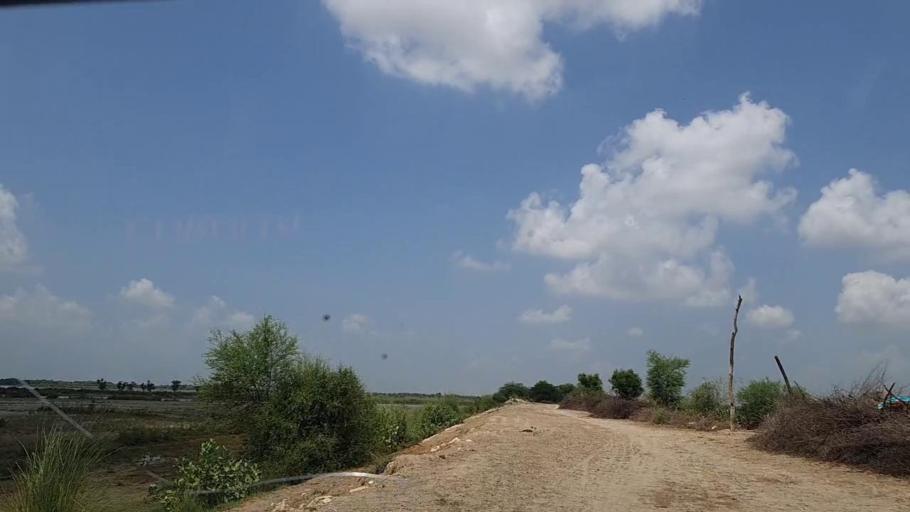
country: PK
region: Sindh
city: Tharu Shah
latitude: 26.9653
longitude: 68.0312
